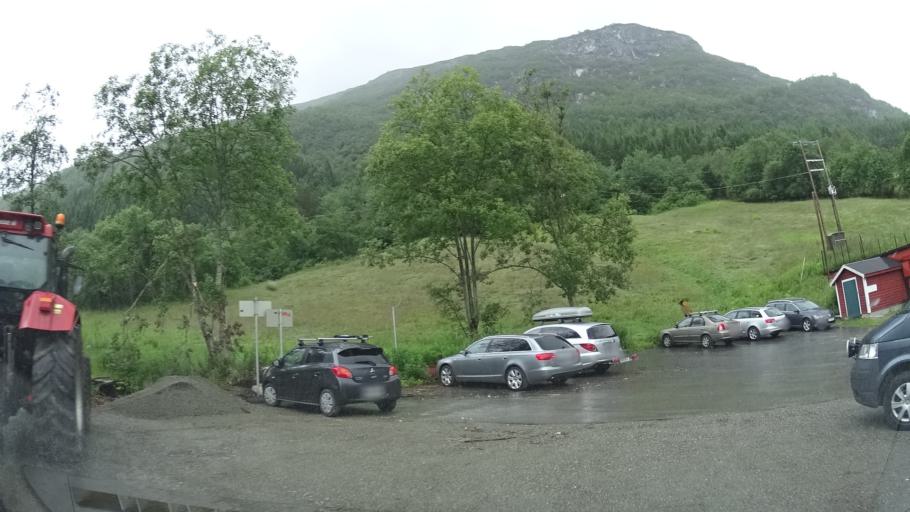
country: NO
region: Sogn og Fjordane
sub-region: Vik
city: Vik
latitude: 60.8360
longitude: 6.6798
